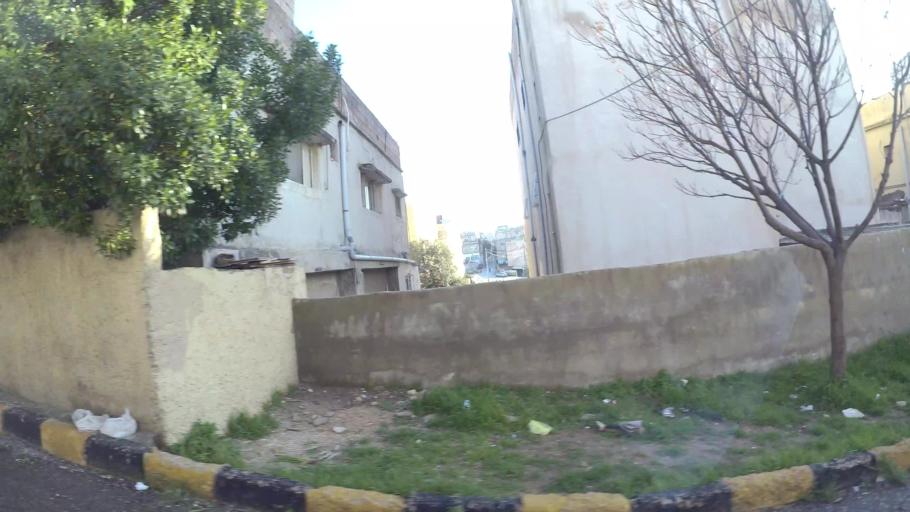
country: JO
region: Amman
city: Al Bunayyat ash Shamaliyah
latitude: 31.9101
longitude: 35.9146
